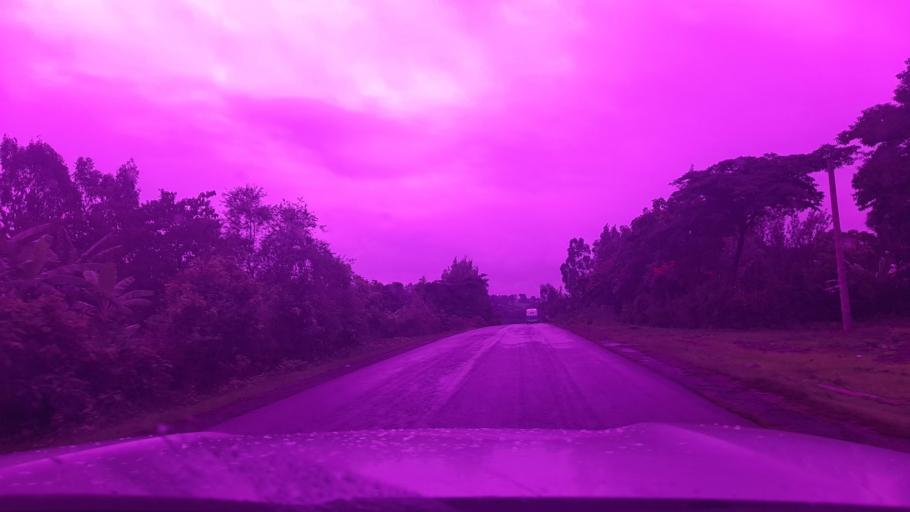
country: ET
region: Oromiya
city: Jima
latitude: 7.8082
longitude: 37.3440
